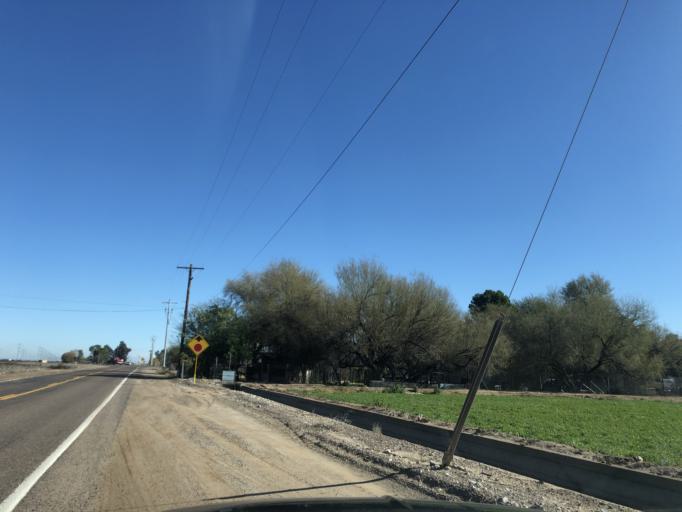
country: US
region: Arizona
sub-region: Maricopa County
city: Goodyear
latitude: 33.3919
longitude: -112.4485
